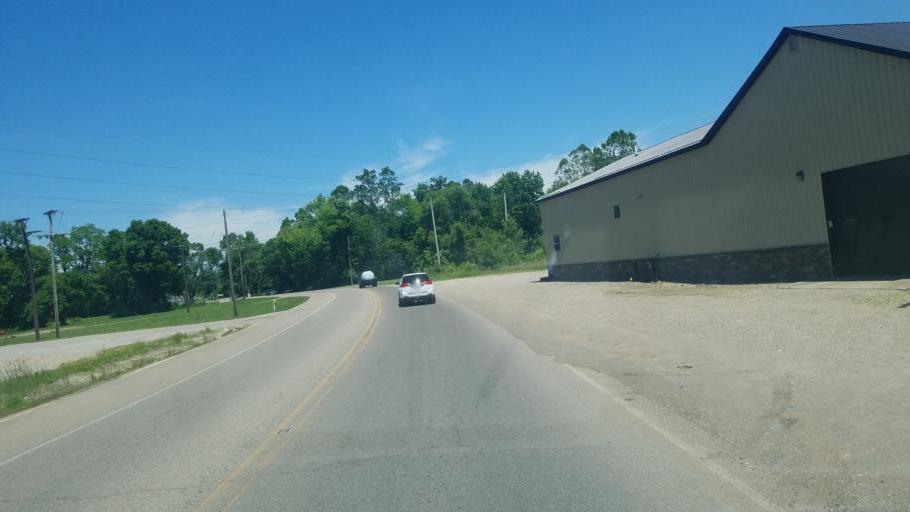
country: US
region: Ohio
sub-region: Coshocton County
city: Coshocton
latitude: 40.2799
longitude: -81.8709
